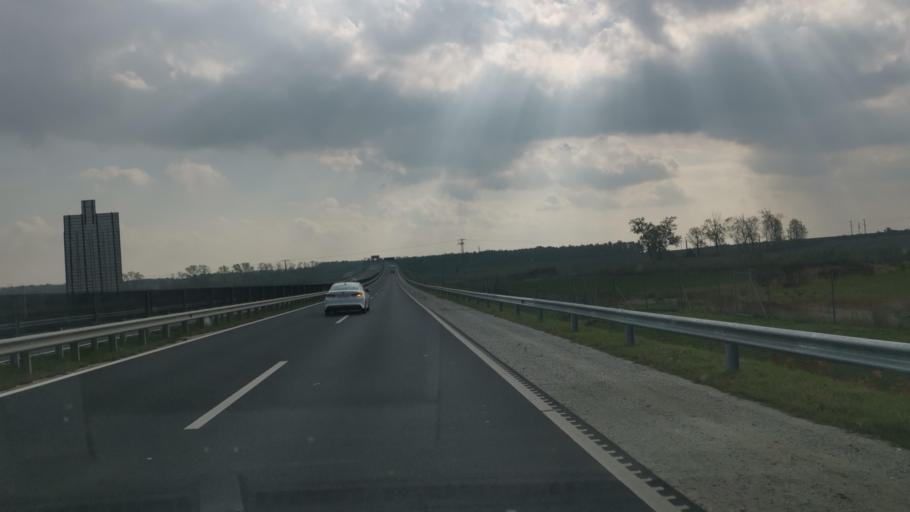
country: AT
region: Burgenland
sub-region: Politischer Bezirk Oberpullendorf
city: Deutschkreutz
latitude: 47.6421
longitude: 16.6278
